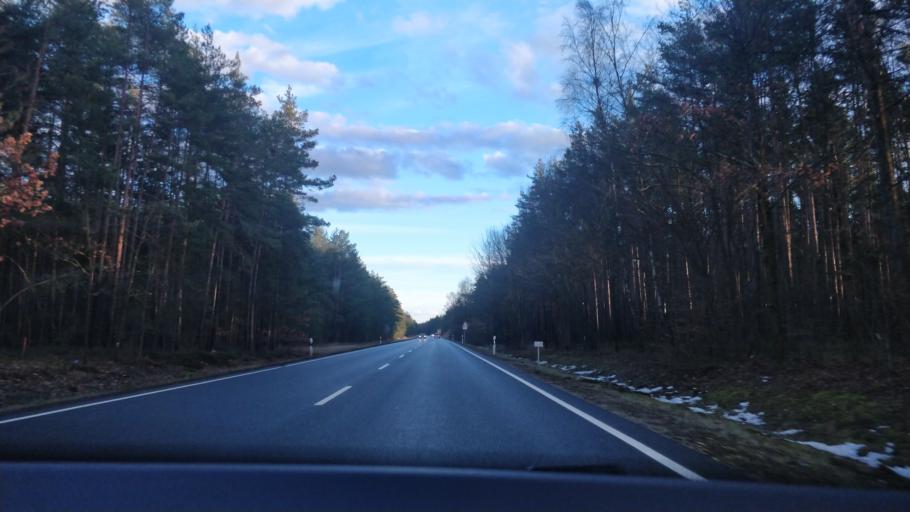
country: DE
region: Bavaria
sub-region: Upper Palatinate
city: Pressath
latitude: 49.7437
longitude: 11.9434
